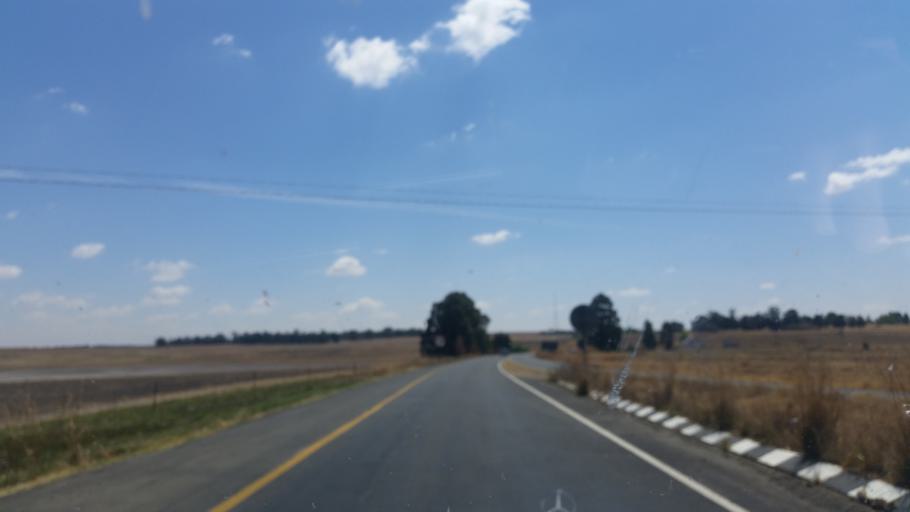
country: ZA
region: Orange Free State
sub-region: Thabo Mofutsanyana District Municipality
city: Reitz
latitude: -28.0823
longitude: 28.6484
